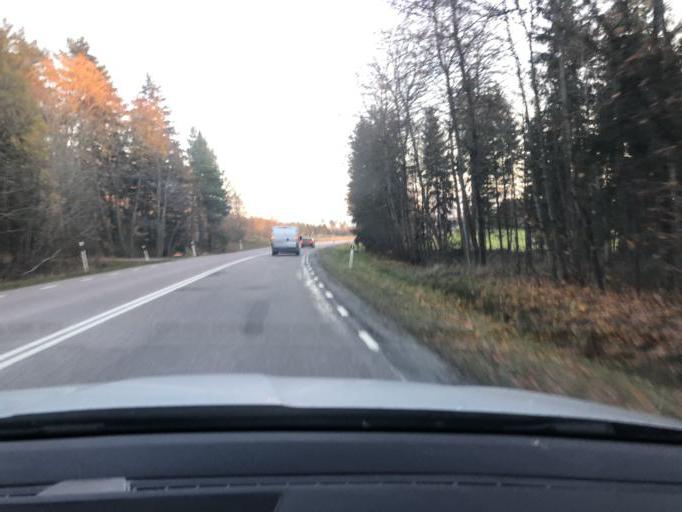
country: SE
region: Soedermanland
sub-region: Strangnas Kommun
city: Akers Styckebruk
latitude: 59.2939
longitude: 17.1060
